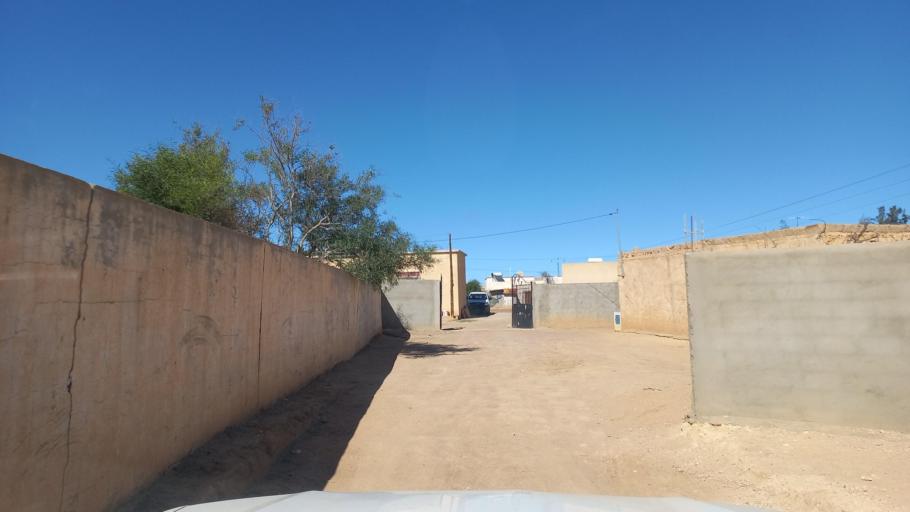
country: TN
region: Al Qasrayn
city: Sbiba
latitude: 35.3621
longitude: 9.0923
